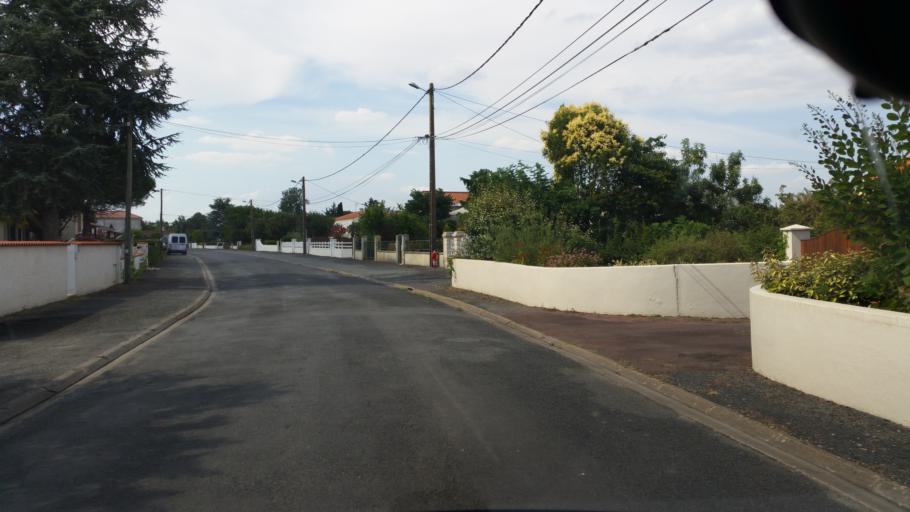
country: FR
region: Poitou-Charentes
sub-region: Departement de la Charente-Maritime
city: Marans
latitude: 46.3053
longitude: -0.9834
